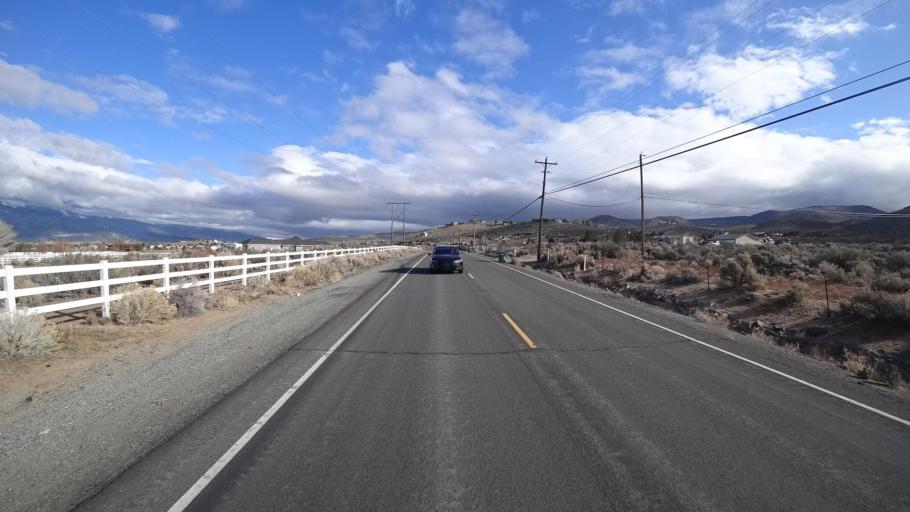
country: US
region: Nevada
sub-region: Carson City
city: Carson City
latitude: 39.2739
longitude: -119.7566
